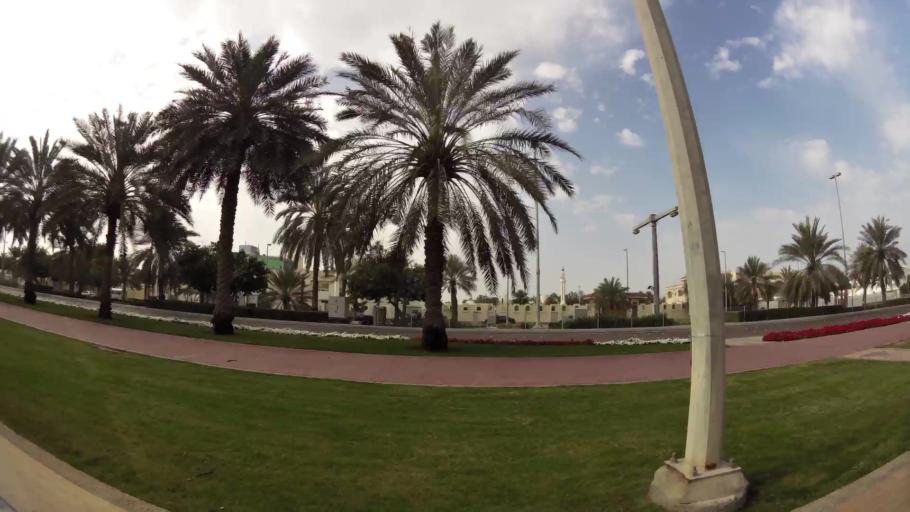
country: AE
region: Abu Dhabi
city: Abu Dhabi
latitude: 24.4346
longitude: 54.3713
